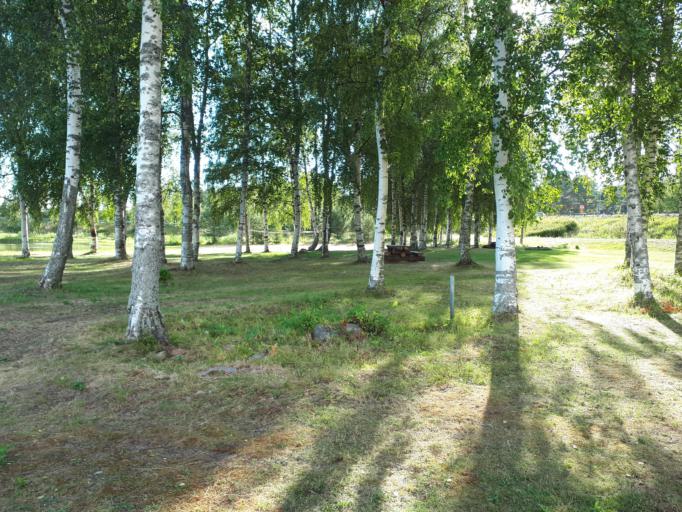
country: FI
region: Northern Ostrobothnia
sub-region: Oulunkaari
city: Ii
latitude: 65.3301
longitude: 25.3808
